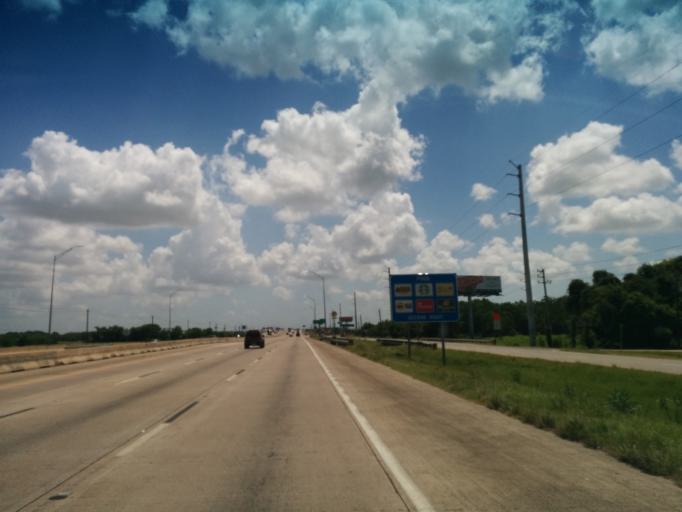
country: US
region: Texas
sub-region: Harris County
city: Highlands
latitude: 29.8008
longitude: -95.0055
